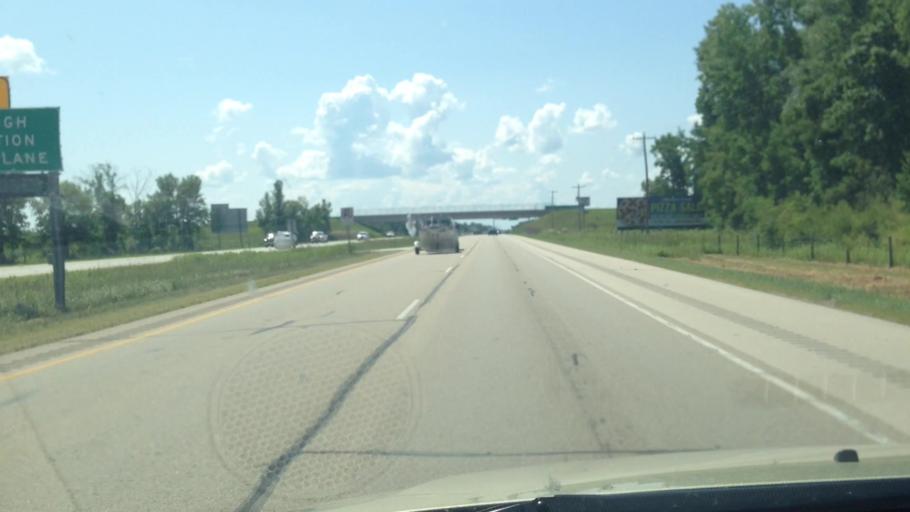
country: US
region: Wisconsin
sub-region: Brown County
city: Suamico
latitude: 44.7534
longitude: -88.0512
